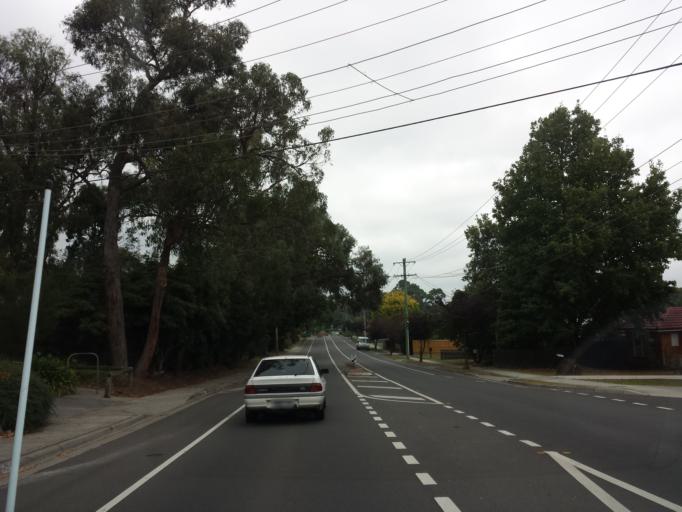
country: AU
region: Victoria
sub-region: Knox
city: The Basin
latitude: -37.8508
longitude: 145.2988
